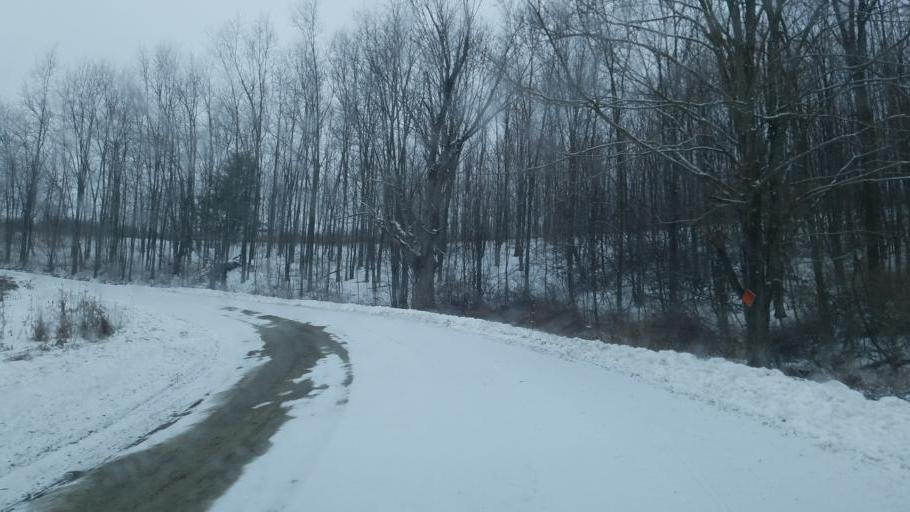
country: US
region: New York
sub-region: Steuben County
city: Canisteo
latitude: 42.1282
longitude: -77.5378
